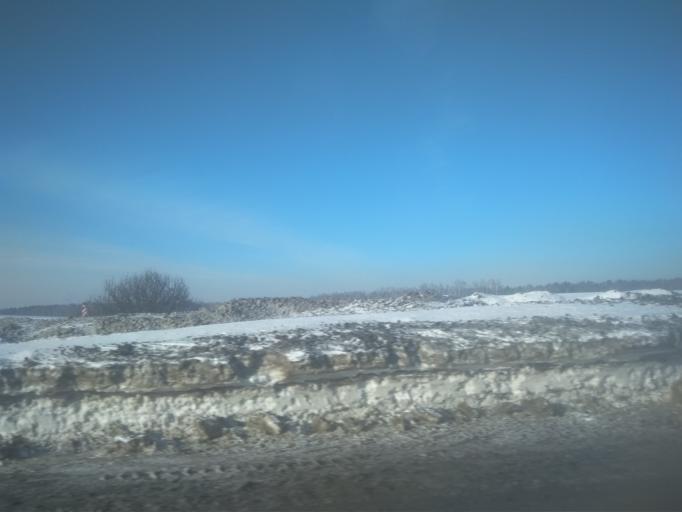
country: RU
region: Moskovskaya
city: Gorki-Leninskiye
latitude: 55.5067
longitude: 37.8350
